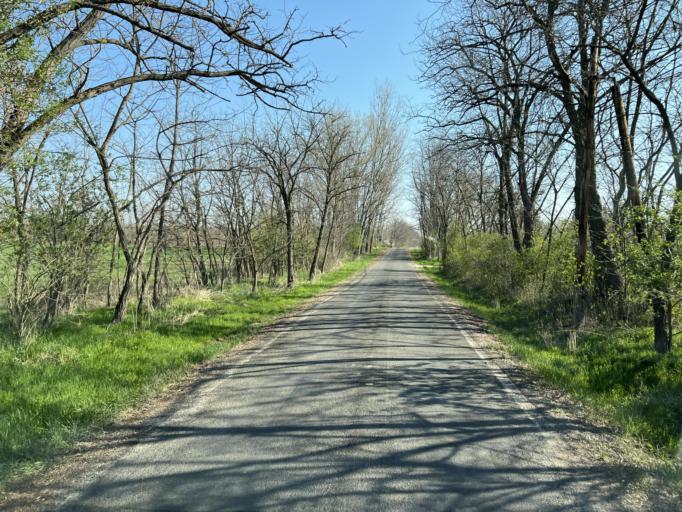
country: SK
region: Nitriansky
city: Sahy
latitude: 48.0338
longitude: 18.8357
